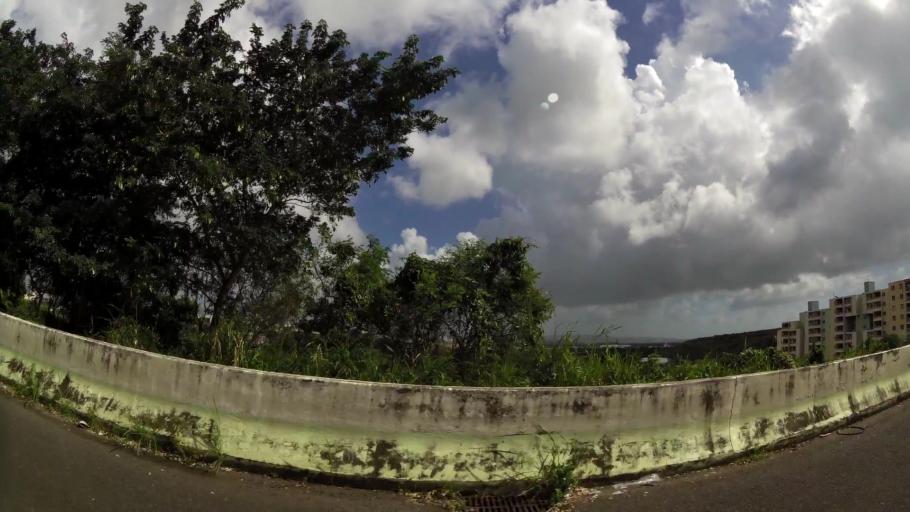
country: MQ
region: Martinique
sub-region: Martinique
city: Le Lamentin
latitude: 14.6154
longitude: -61.0409
